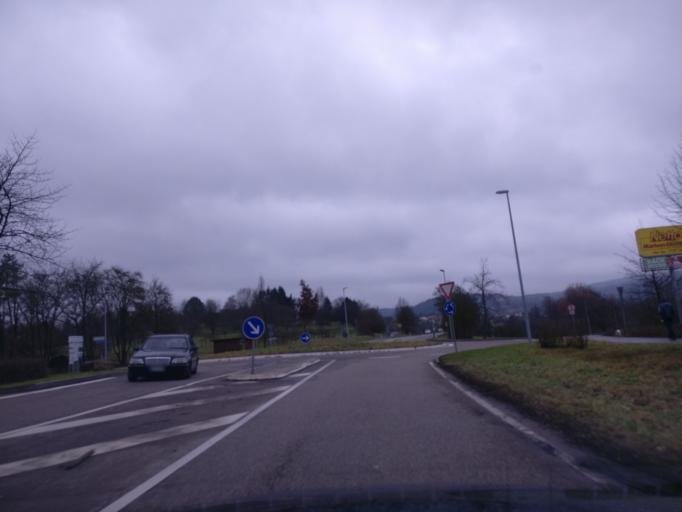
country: DE
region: Baden-Wuerttemberg
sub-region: Regierungsbezirk Stuttgart
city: Rudersberg
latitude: 48.8467
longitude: 9.5406
